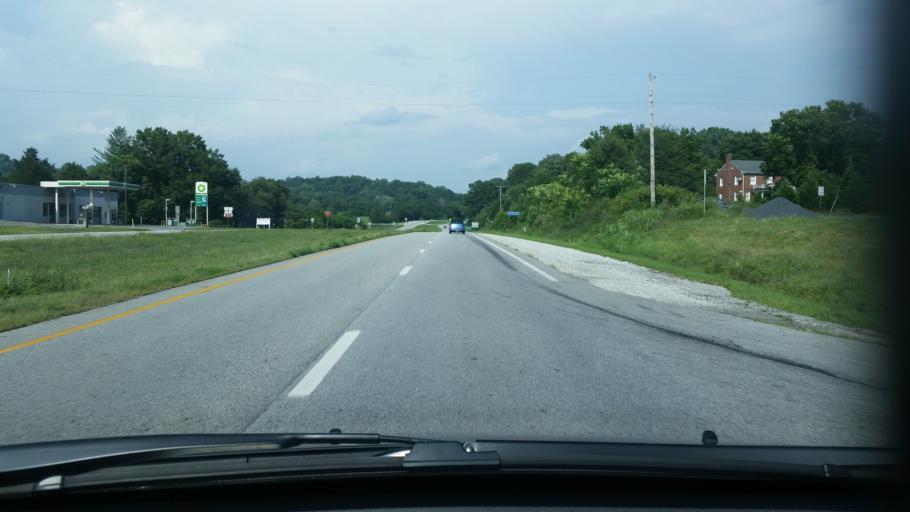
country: US
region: Virginia
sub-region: Nelson County
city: Lovingston
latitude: 37.7082
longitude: -78.9329
